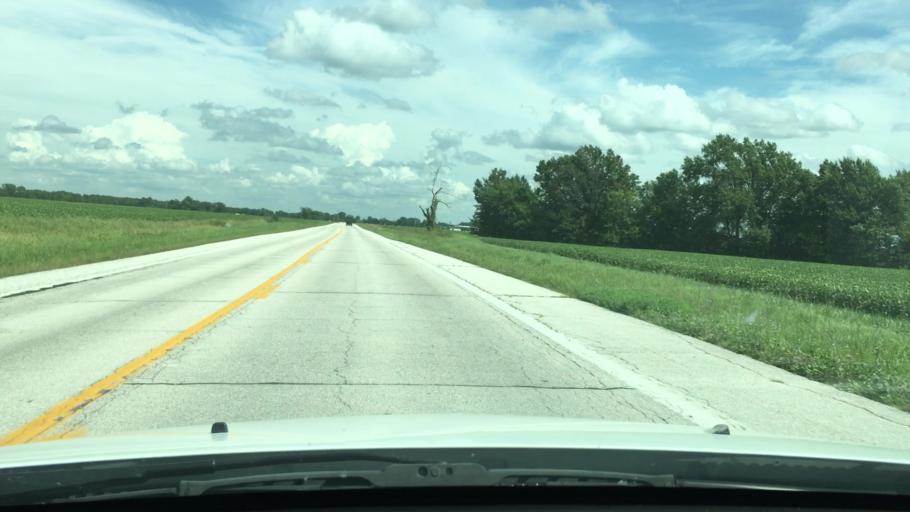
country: US
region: Missouri
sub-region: Audrain County
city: Vandalia
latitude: 39.3396
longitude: -91.4194
